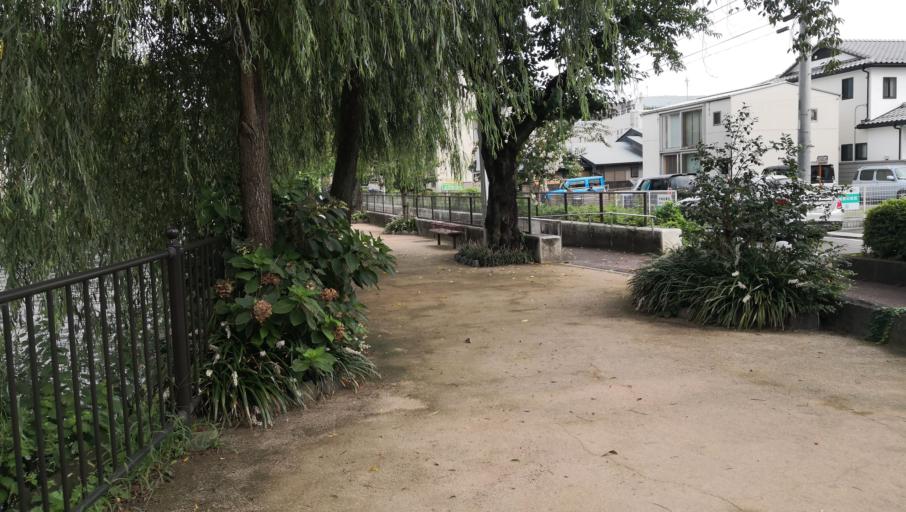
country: JP
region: Gunma
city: Maebashi-shi
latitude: 36.3954
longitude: 139.0674
